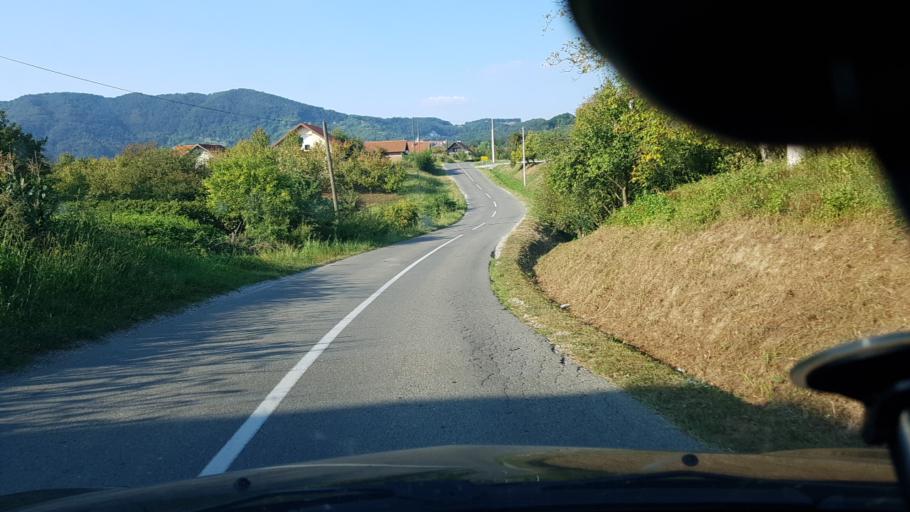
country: SI
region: Bistrica ob Sotli
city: Bistrica ob Sotli
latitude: 46.0289
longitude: 15.7319
